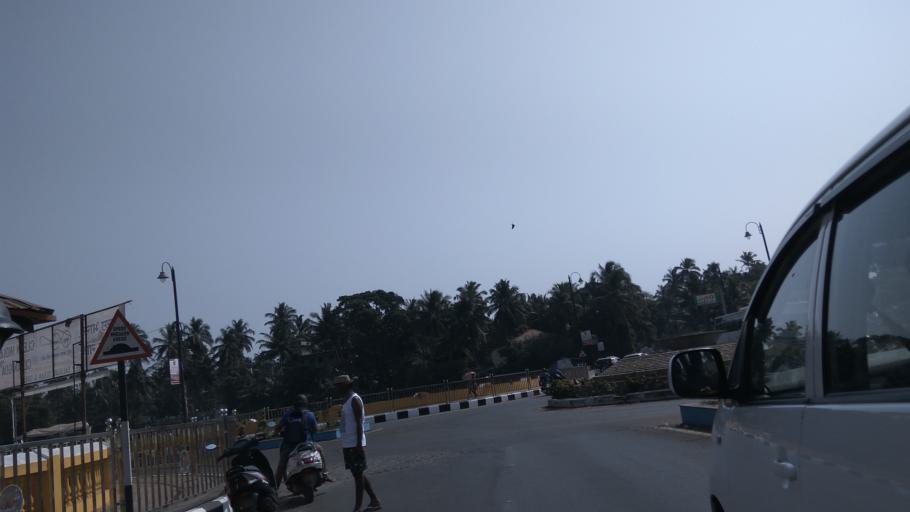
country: IN
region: Goa
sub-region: North Goa
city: Saligao
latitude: 15.5462
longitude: 73.7889
